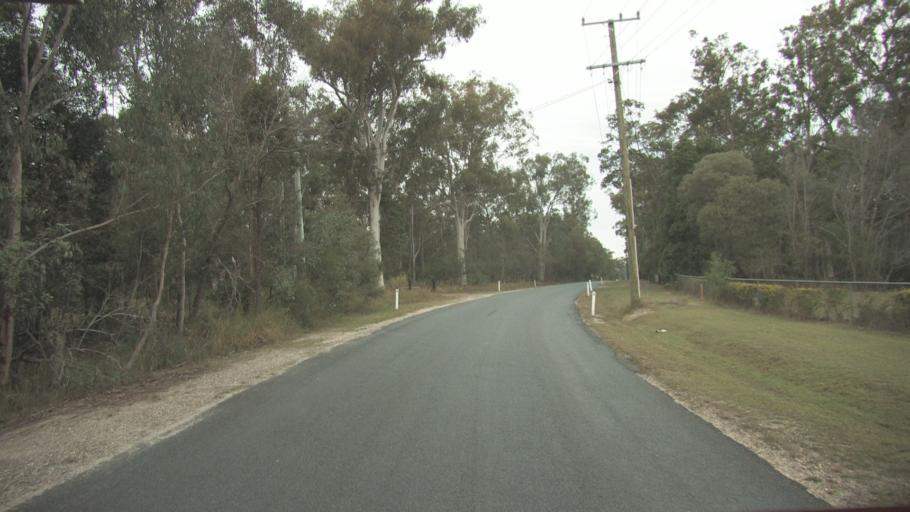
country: AU
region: Queensland
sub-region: Logan
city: Chambers Flat
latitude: -27.7784
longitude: 153.1169
